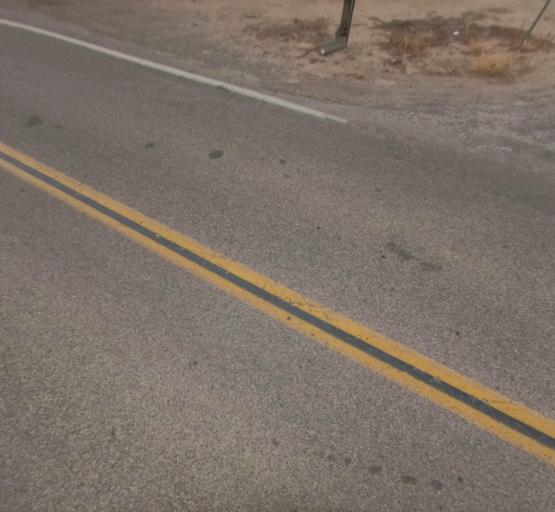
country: US
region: California
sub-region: Madera County
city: Fairmead
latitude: 37.0184
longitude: -120.2296
